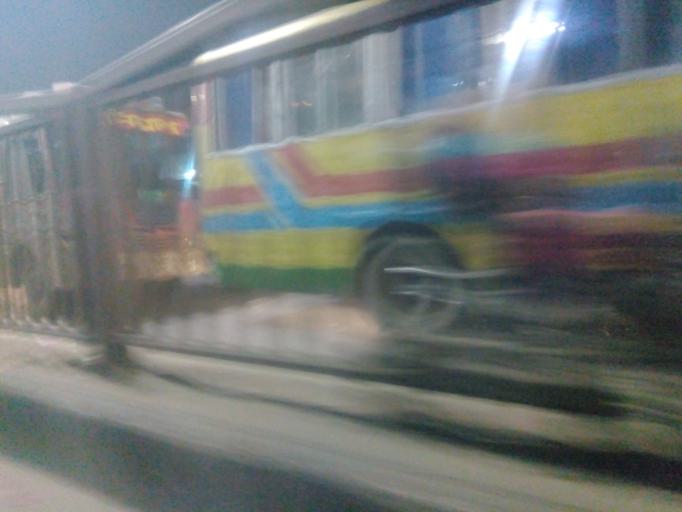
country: BD
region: Dhaka
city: Paltan
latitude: 23.7242
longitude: 90.4119
